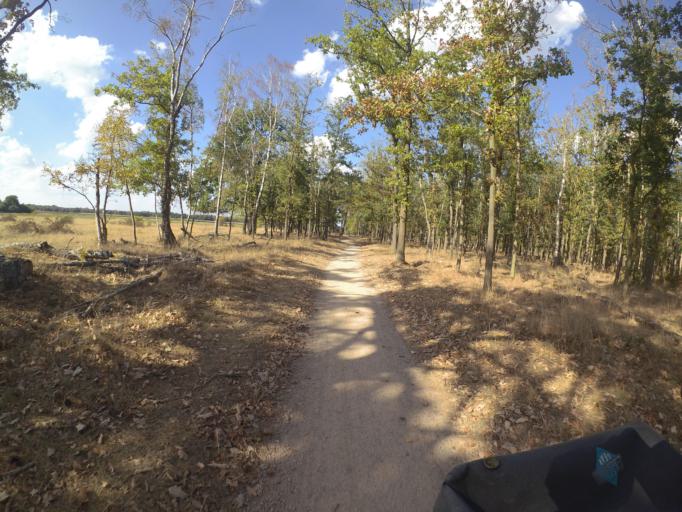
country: NL
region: Overijssel
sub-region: Gemeente Hof van Twente
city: Markelo
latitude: 52.2697
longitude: 6.5050
